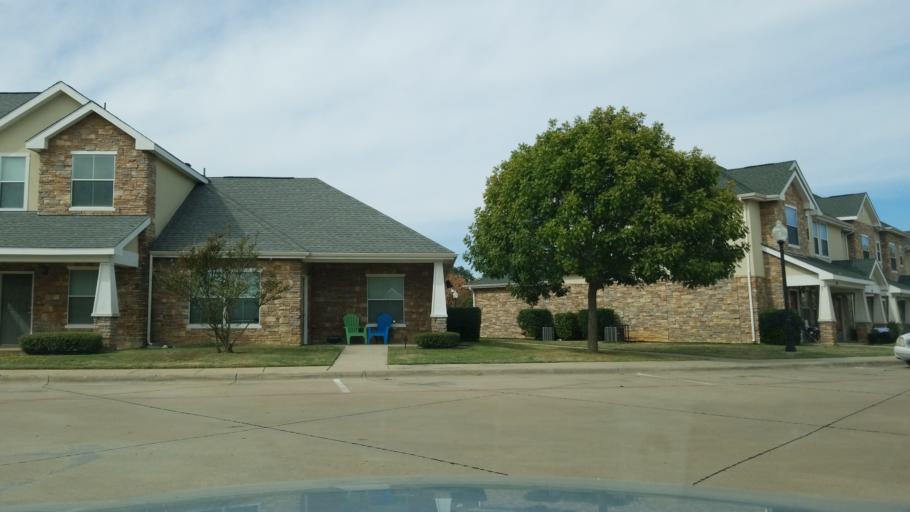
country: US
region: Texas
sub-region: Dallas County
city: Dallas
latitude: 32.7759
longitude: -96.7362
